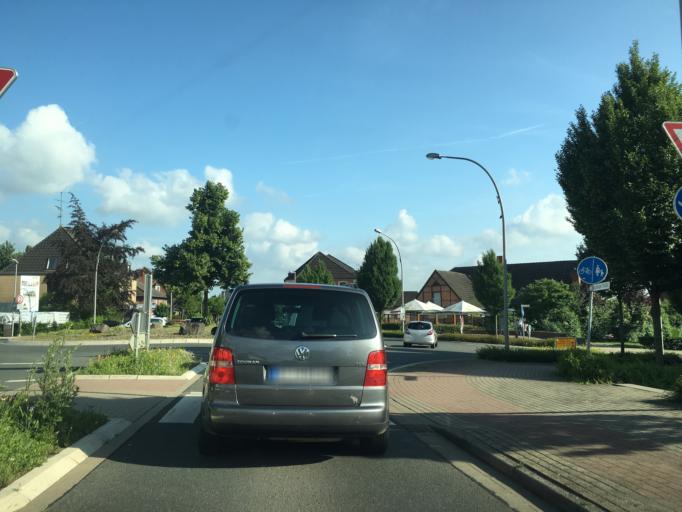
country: DE
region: North Rhine-Westphalia
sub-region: Regierungsbezirk Munster
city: Altenberge
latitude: 52.0461
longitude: 7.4652
